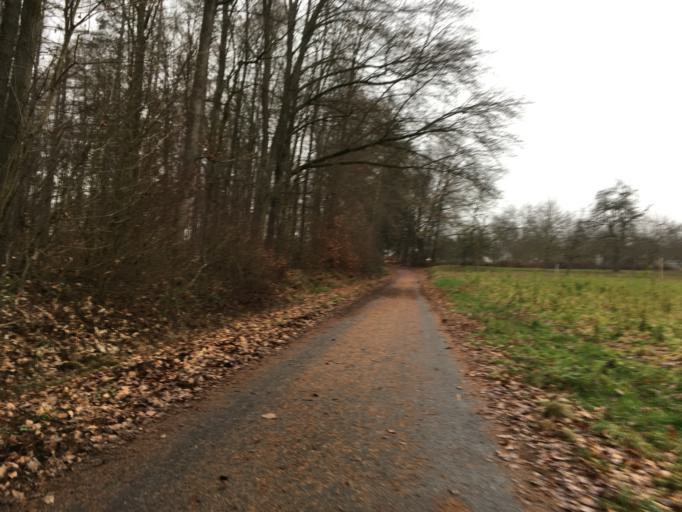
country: DE
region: Baden-Wuerttemberg
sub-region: Karlsruhe Region
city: Konigsbach-Stein
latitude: 48.9480
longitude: 8.5184
